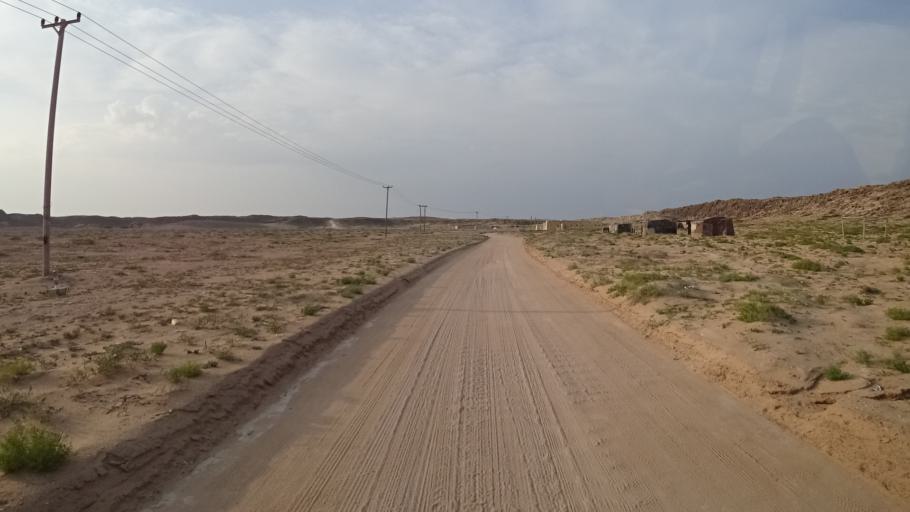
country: OM
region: Ash Sharqiyah
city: Sur
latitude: 22.4454
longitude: 59.8270
